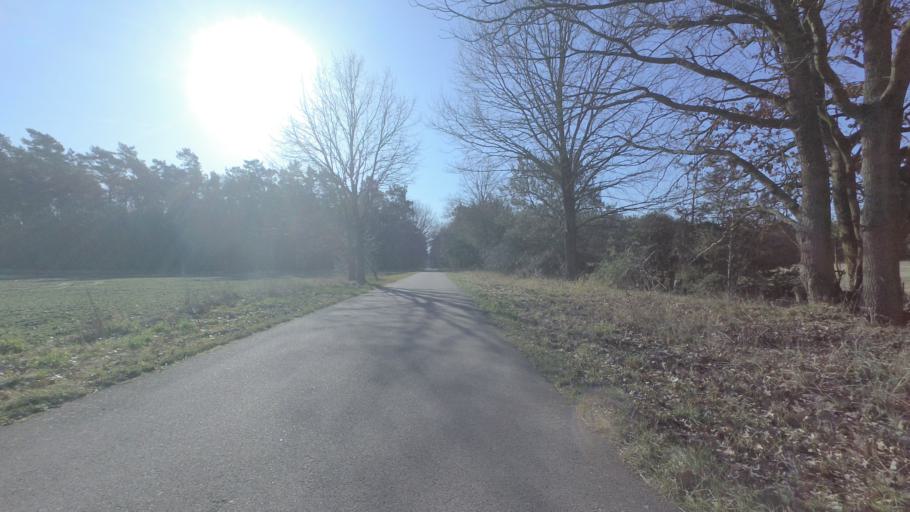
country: DE
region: Brandenburg
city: Juterbog
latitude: 52.0308
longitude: 13.1315
